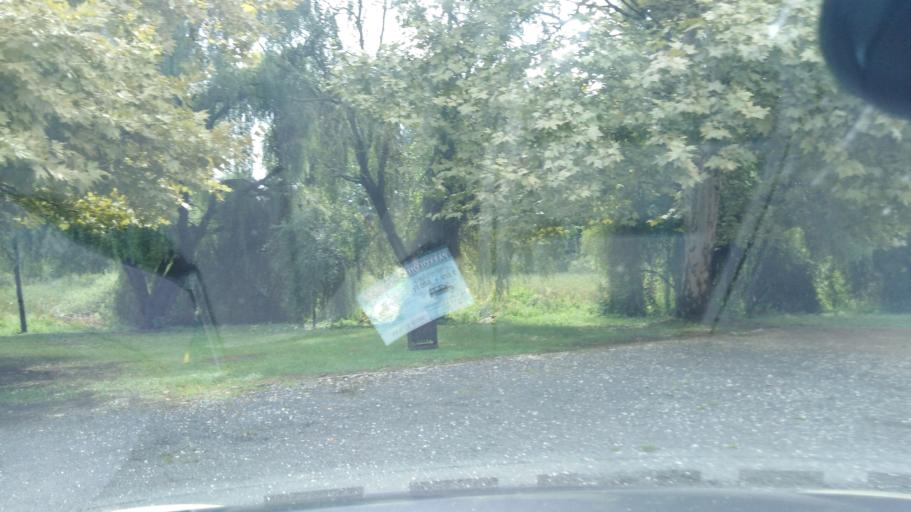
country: HU
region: Zala
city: Zalakomar
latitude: 46.6152
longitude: 17.1686
